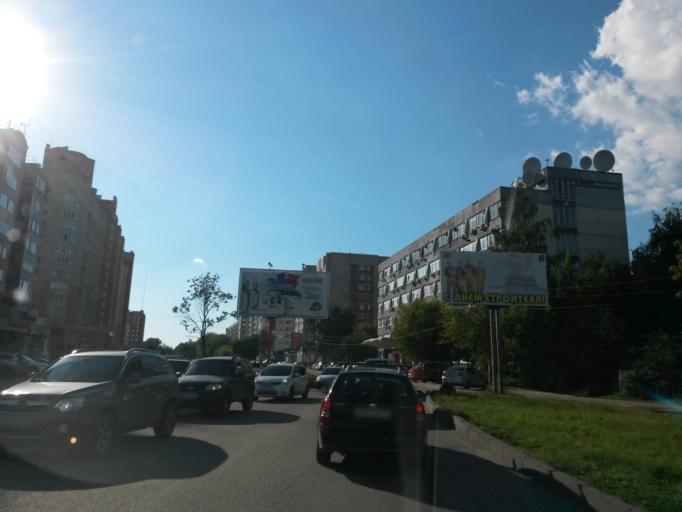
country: RU
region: Ivanovo
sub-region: Gorod Ivanovo
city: Ivanovo
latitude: 56.9816
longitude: 40.9790
